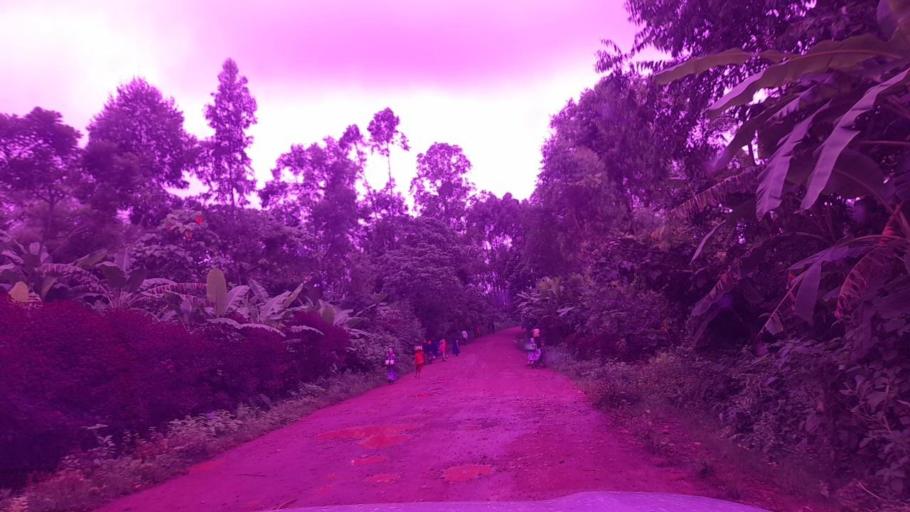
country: ET
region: Southern Nations, Nationalities, and People's Region
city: Bonga
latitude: 7.5845
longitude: 36.0170
